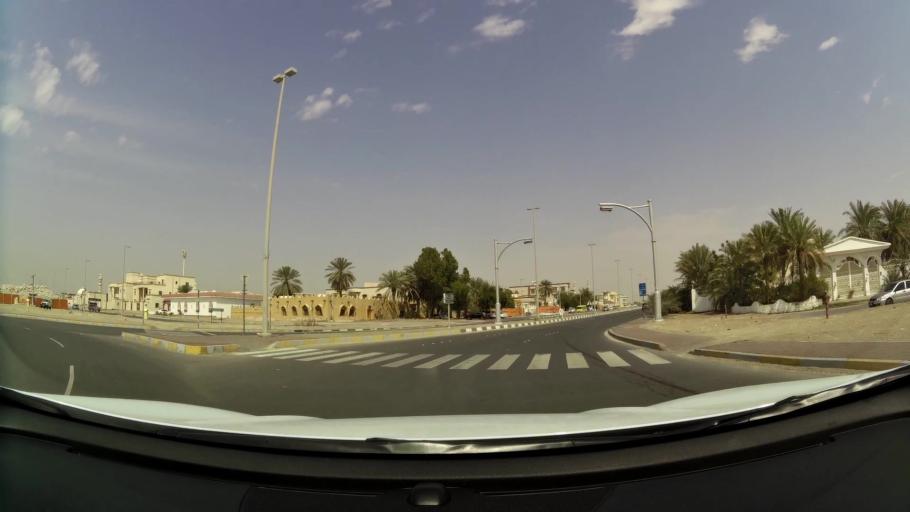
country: AE
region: Abu Dhabi
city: Abu Dhabi
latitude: 24.2945
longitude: 54.6434
